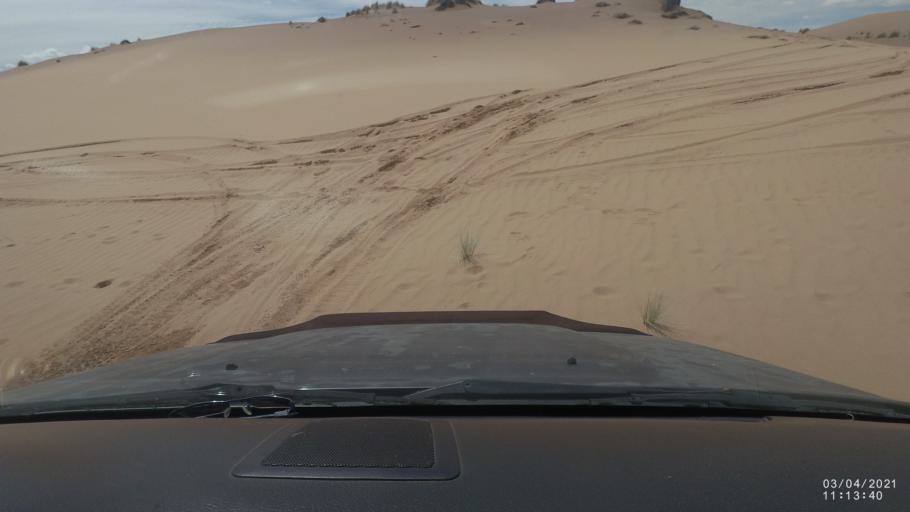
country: BO
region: Oruro
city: Poopo
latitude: -18.7045
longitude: -67.5169
